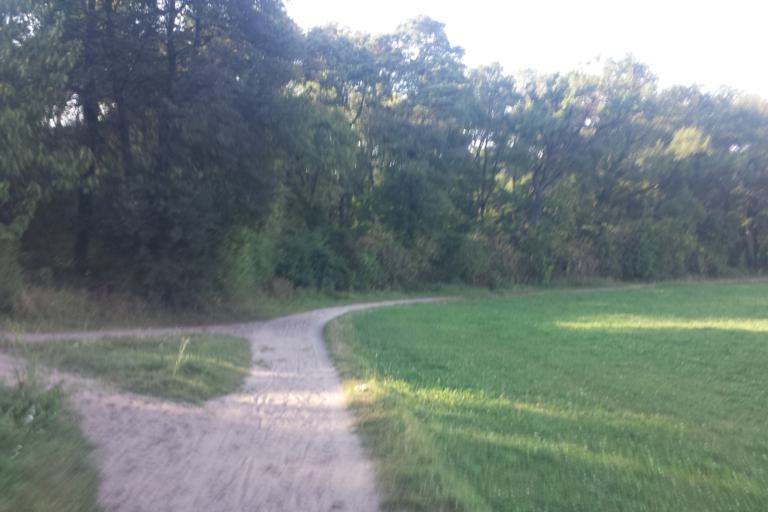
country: DE
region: Baden-Wuerttemberg
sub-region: Karlsruhe Region
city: Bruhl
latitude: 49.4276
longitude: 8.5579
